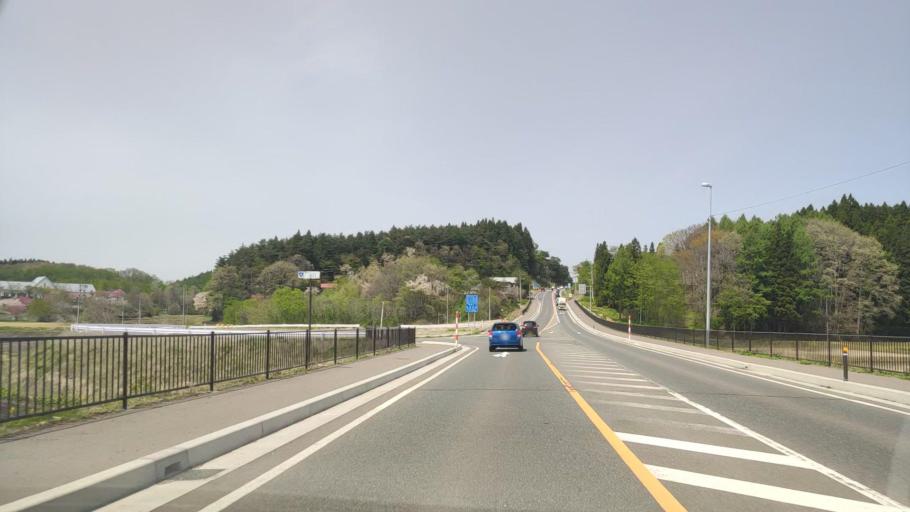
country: JP
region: Aomori
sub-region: Misawa Shi
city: Inuotose
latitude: 40.6639
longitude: 141.1875
